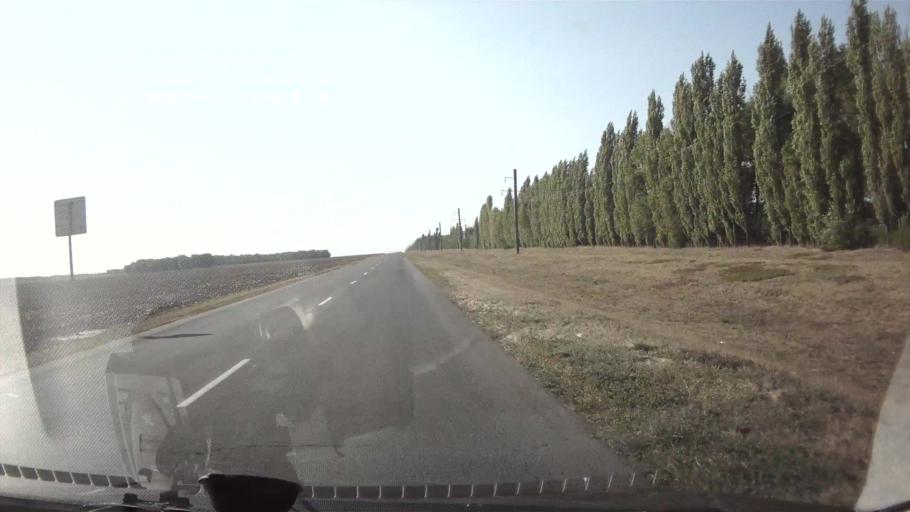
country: RU
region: Rostov
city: Tselina
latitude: 46.5340
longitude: 40.8998
